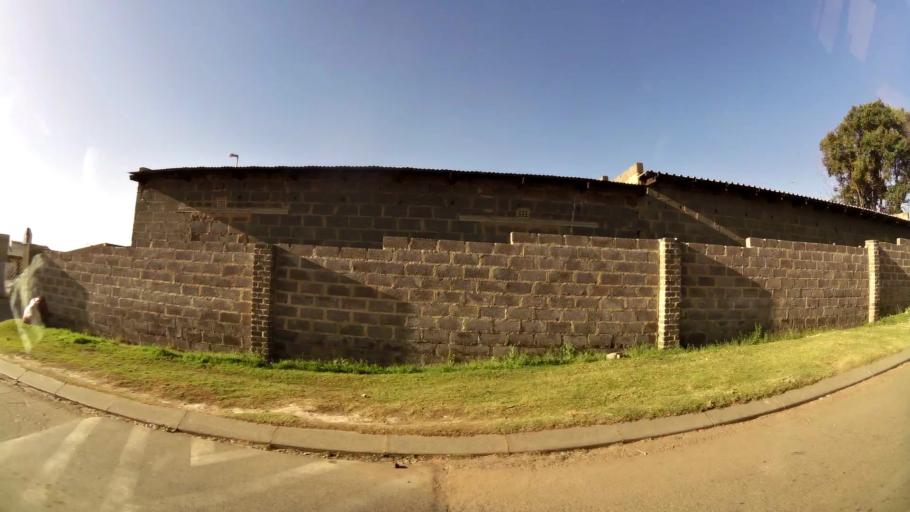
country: ZA
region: Gauteng
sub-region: Ekurhuleni Metropolitan Municipality
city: Tembisa
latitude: -26.0206
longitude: 28.2225
